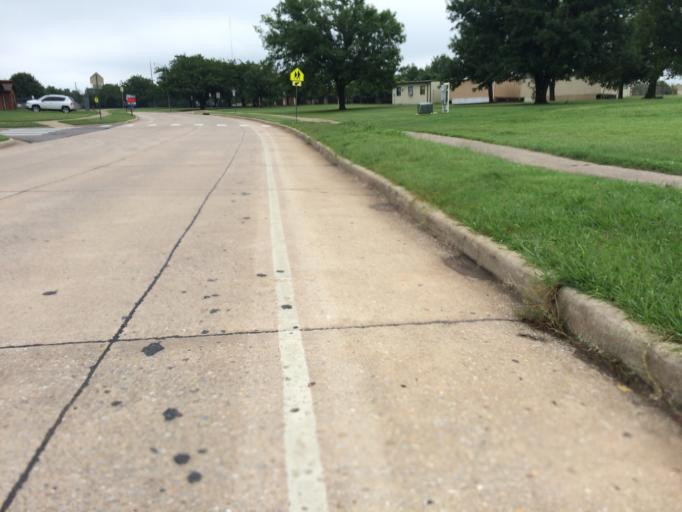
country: US
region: Oklahoma
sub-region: Cleveland County
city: Hall Park
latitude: 35.2146
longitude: -97.4124
